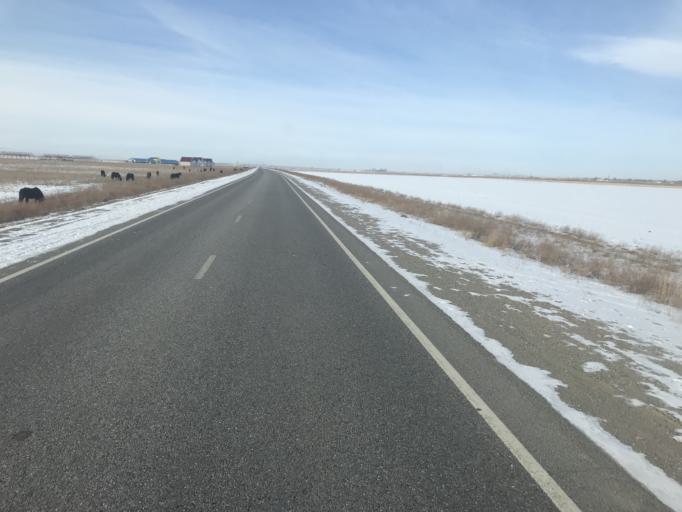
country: KZ
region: Zhambyl
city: Sarykemer
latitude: 43.0510
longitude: 71.4772
